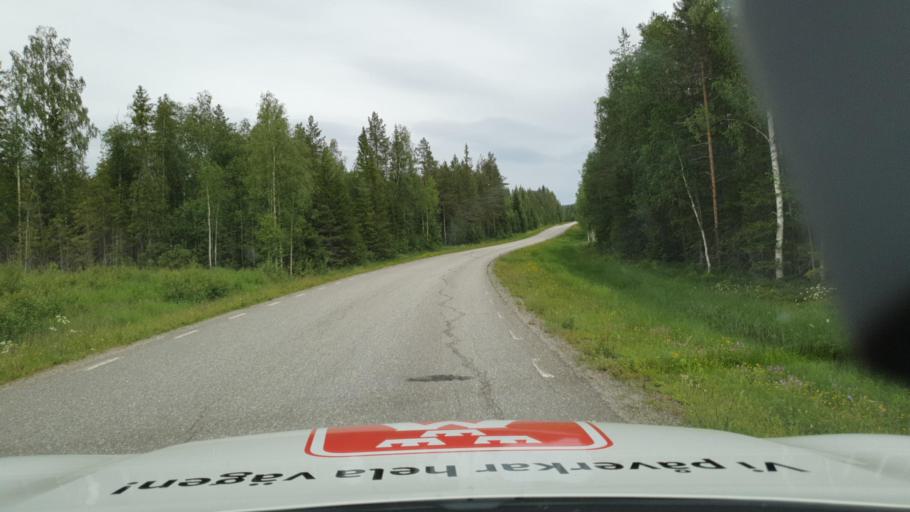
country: SE
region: Vaesterbotten
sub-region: Skelleftea Kommun
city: Burtraesk
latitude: 64.2948
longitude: 20.6456
